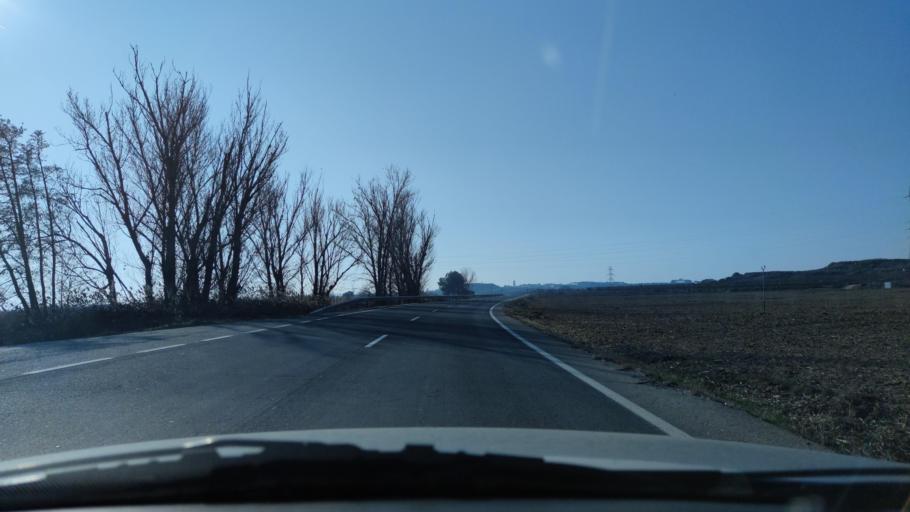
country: ES
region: Catalonia
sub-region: Provincia de Lleida
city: Albesa
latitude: 41.7118
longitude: 0.6391
